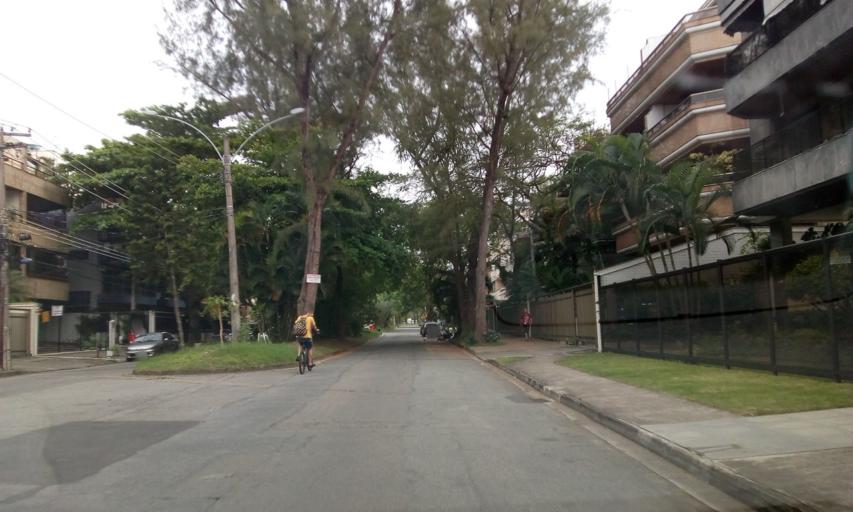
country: BR
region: Rio de Janeiro
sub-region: Nilopolis
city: Nilopolis
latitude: -23.0177
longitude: -43.4544
